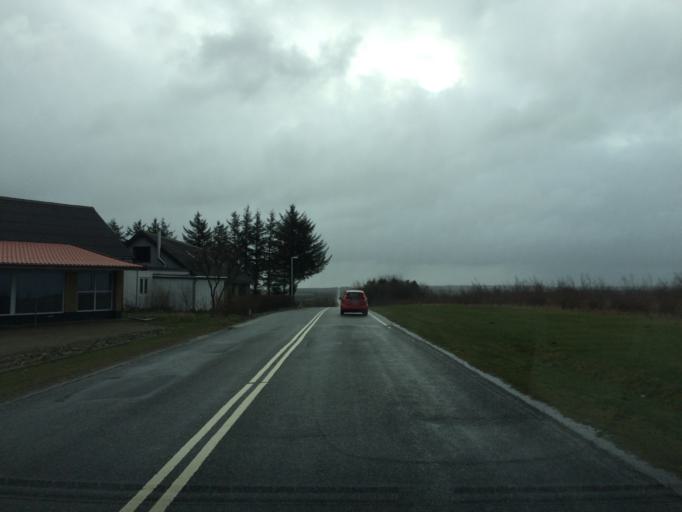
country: DK
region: Central Jutland
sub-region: Ringkobing-Skjern Kommune
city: Videbaek
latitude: 56.1923
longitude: 8.5752
